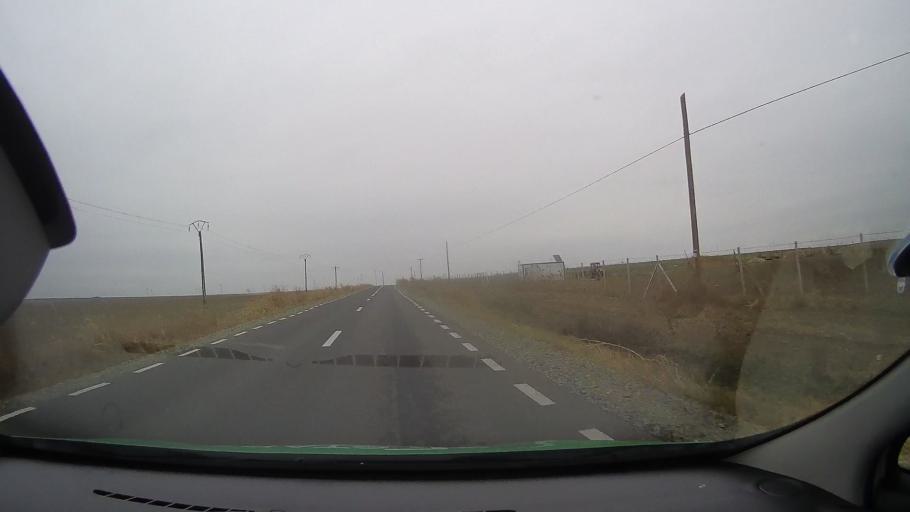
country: RO
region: Constanta
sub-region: Comuna Tortoman
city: Tortoman
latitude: 44.3551
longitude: 28.2131
